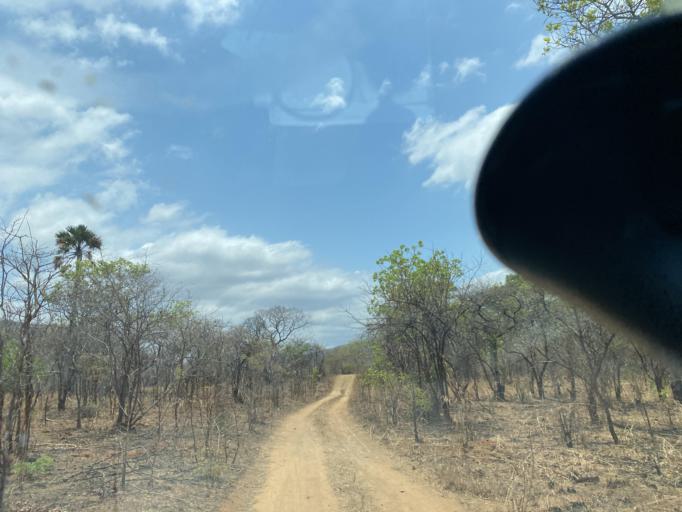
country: ZM
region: Lusaka
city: Luangwa
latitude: -15.1816
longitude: 29.7218
